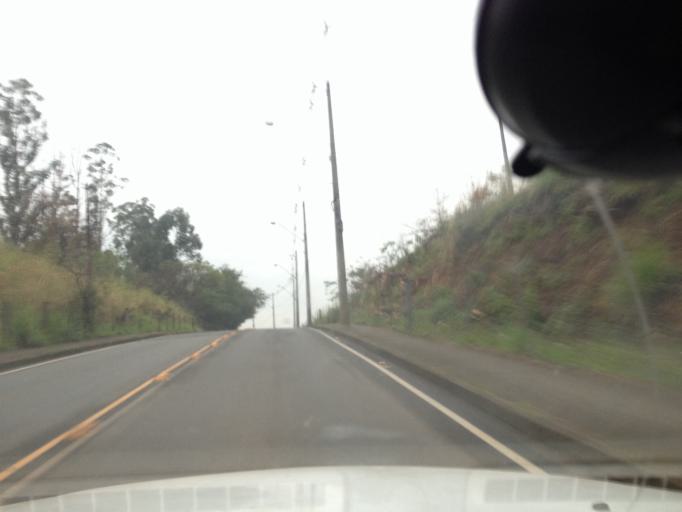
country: BR
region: Sao Paulo
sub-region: Salto
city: Salto
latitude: -23.2046
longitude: -47.2729
